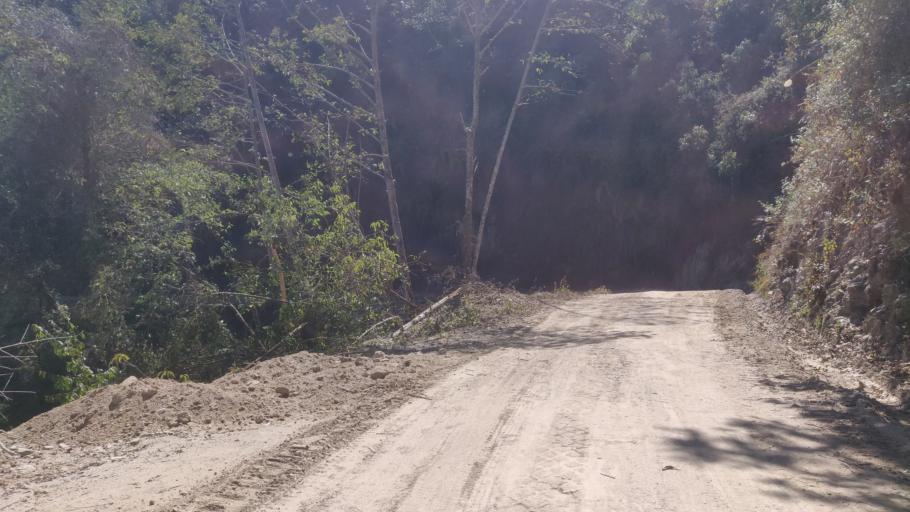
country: NP
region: Central Region
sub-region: Bagmati Zone
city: Nagarkot
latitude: 27.7842
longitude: 85.4818
